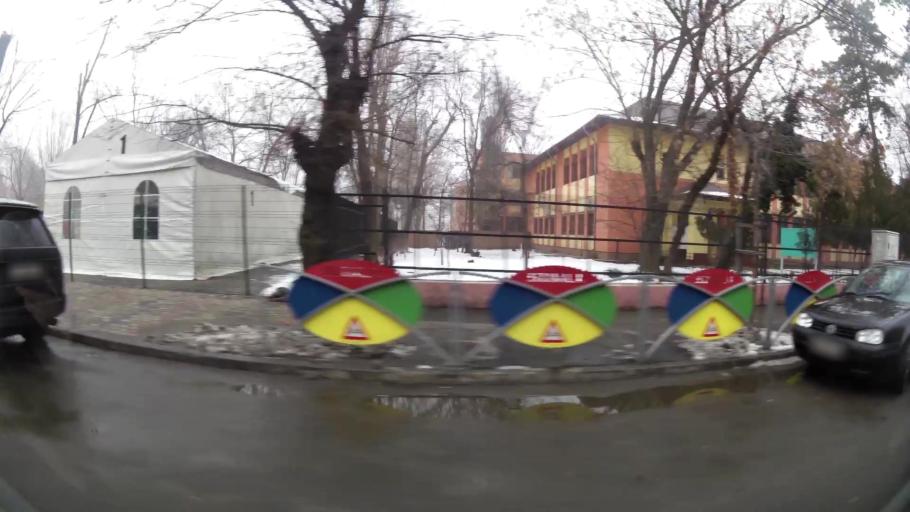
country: RO
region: Ilfov
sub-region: Comuna Chiajna
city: Rosu
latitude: 44.4616
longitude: 26.0451
